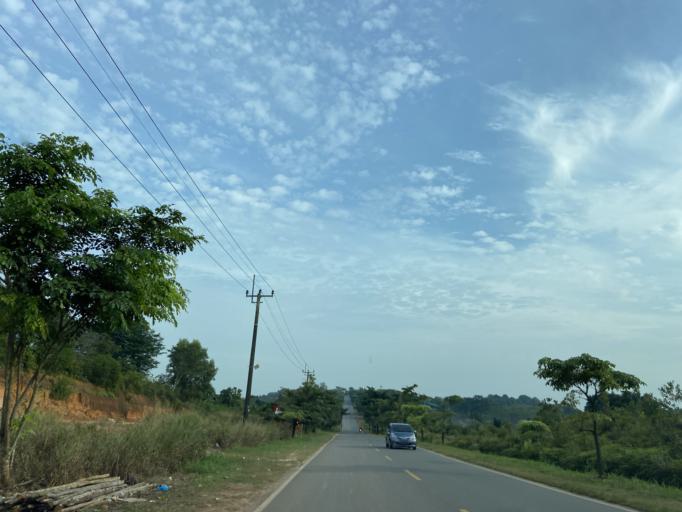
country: ID
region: Riau Islands
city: Tanjungpinang
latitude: 0.9204
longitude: 104.1179
